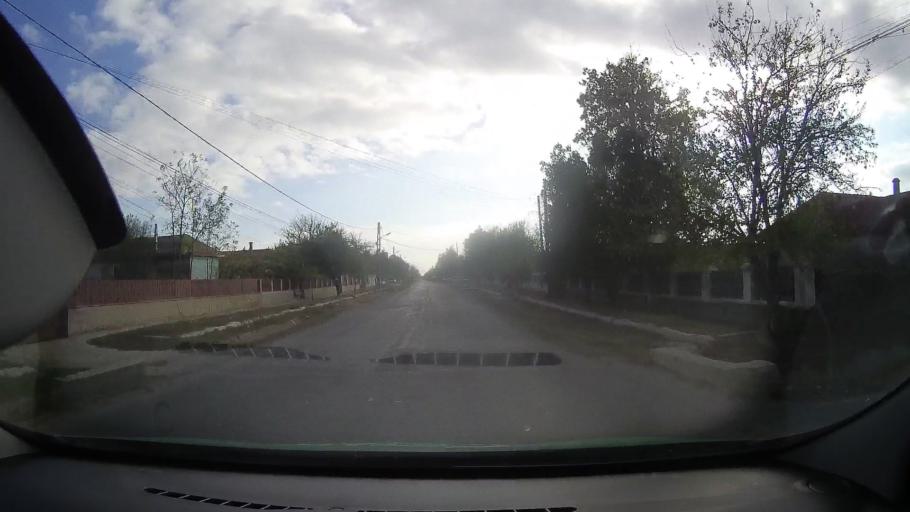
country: RO
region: Constanta
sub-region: Comuna Corbu
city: Corbu
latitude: 44.4168
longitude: 28.6609
